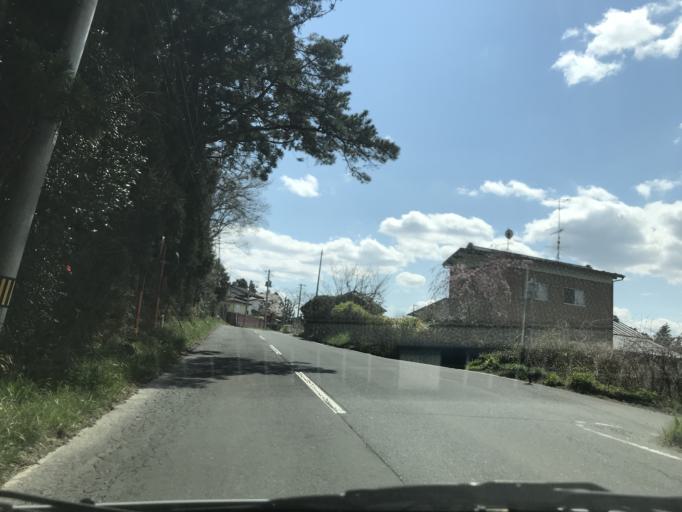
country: JP
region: Miyagi
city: Wakuya
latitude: 38.6363
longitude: 141.2267
